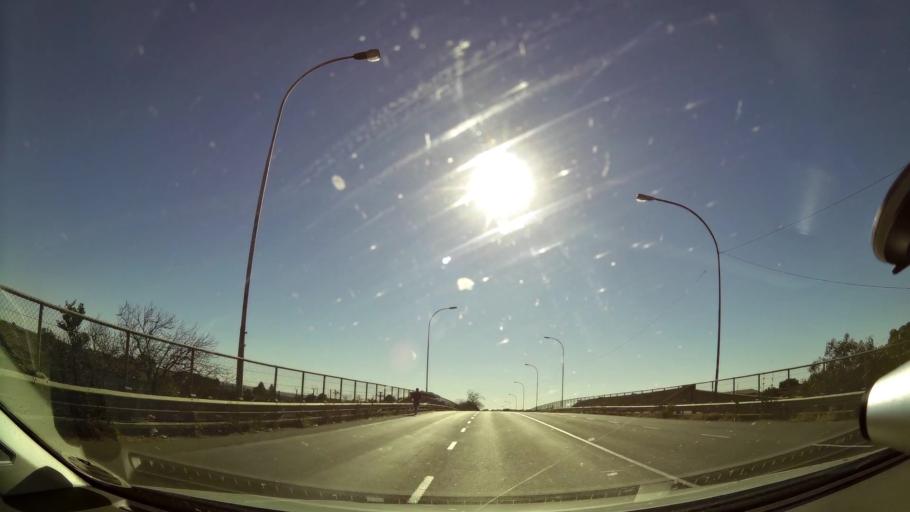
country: ZA
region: Northern Cape
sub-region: Frances Baard District Municipality
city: Kimberley
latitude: -28.7254
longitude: 24.7689
